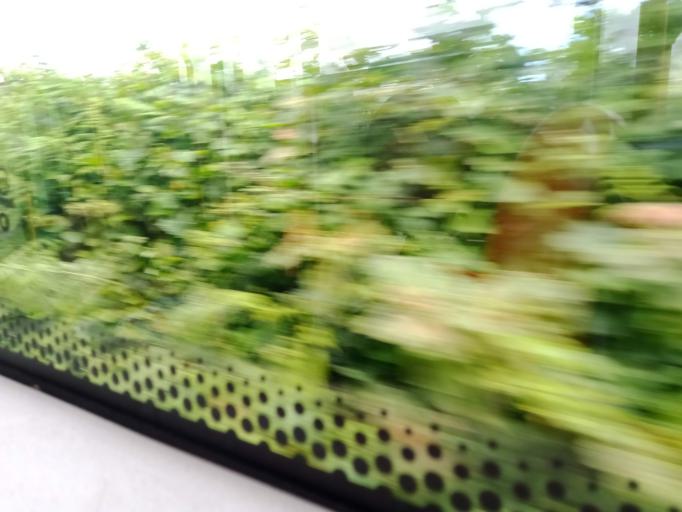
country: GB
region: Wales
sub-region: Anglesey
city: Llangoed
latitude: 53.2969
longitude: -4.0692
